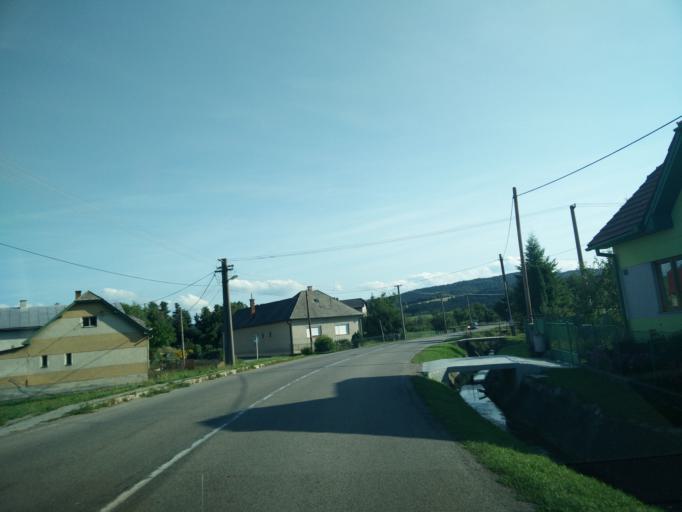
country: SK
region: Nitriansky
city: Handlova
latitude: 48.8835
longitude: 18.7474
